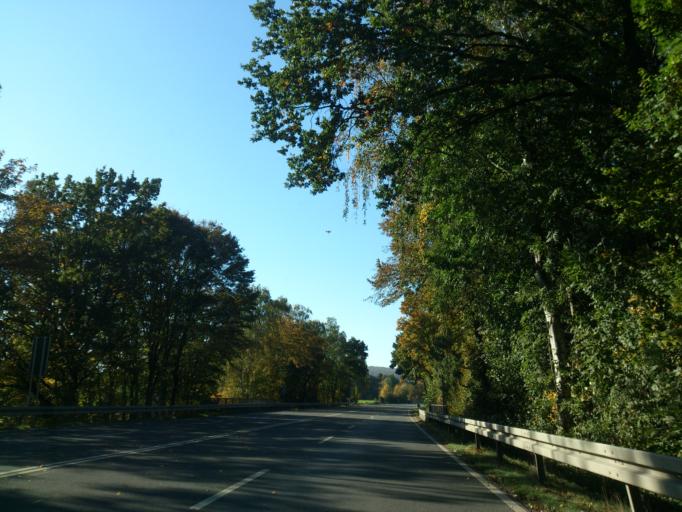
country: DE
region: Hesse
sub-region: Regierungsbezirk Kassel
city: Zierenberg
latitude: 51.4318
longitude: 9.3245
